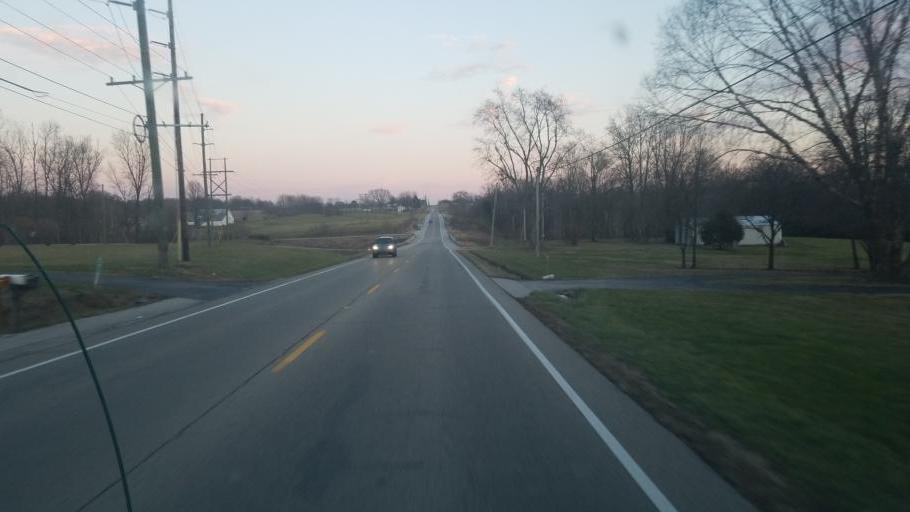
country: US
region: Indiana
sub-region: Lawrence County
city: Bedford
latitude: 38.8753
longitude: -86.3845
